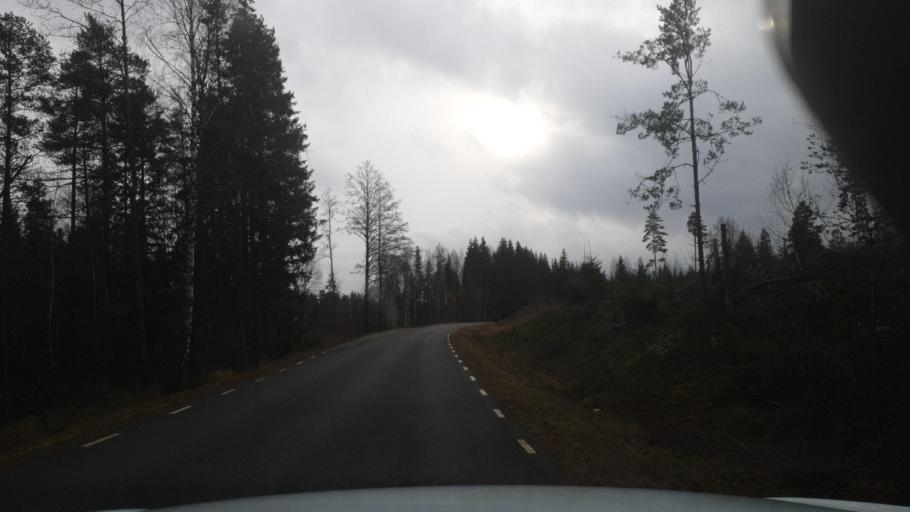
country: SE
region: Vaermland
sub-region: Arvika Kommun
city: Arvika
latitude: 59.5368
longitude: 12.3953
